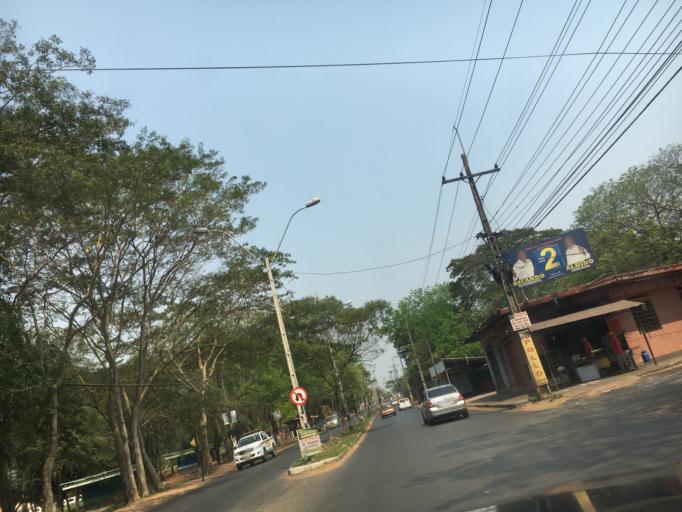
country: PY
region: Central
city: Villa Elisa
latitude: -25.3785
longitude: -57.5848
